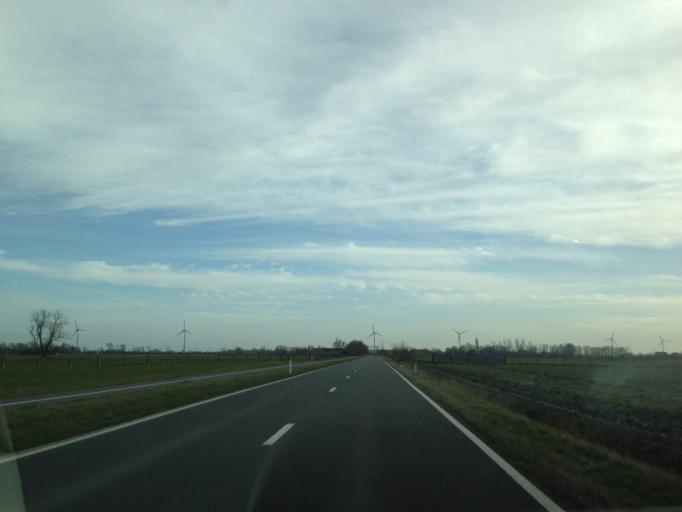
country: BE
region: Flanders
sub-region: Provincie West-Vlaanderen
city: Gistel
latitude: 51.1878
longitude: 2.9618
